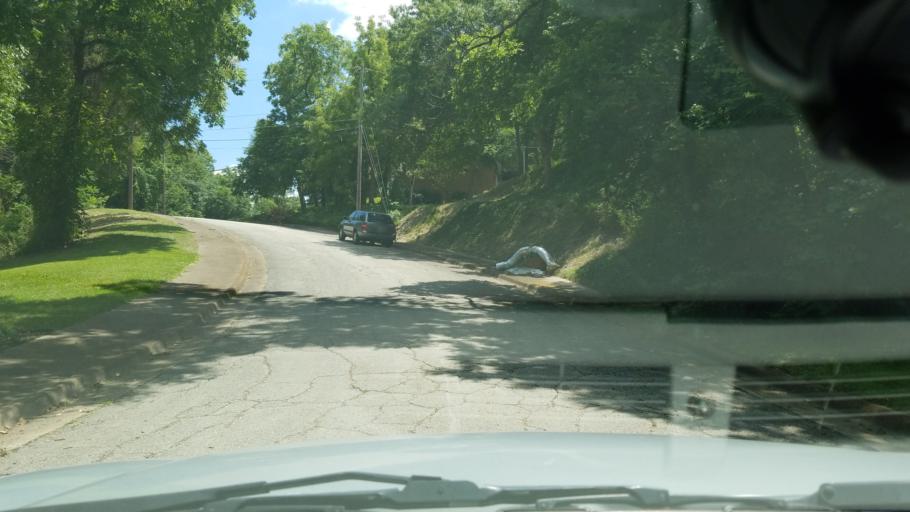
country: US
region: Texas
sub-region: Dallas County
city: Cockrell Hill
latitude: 32.6933
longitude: -96.8632
